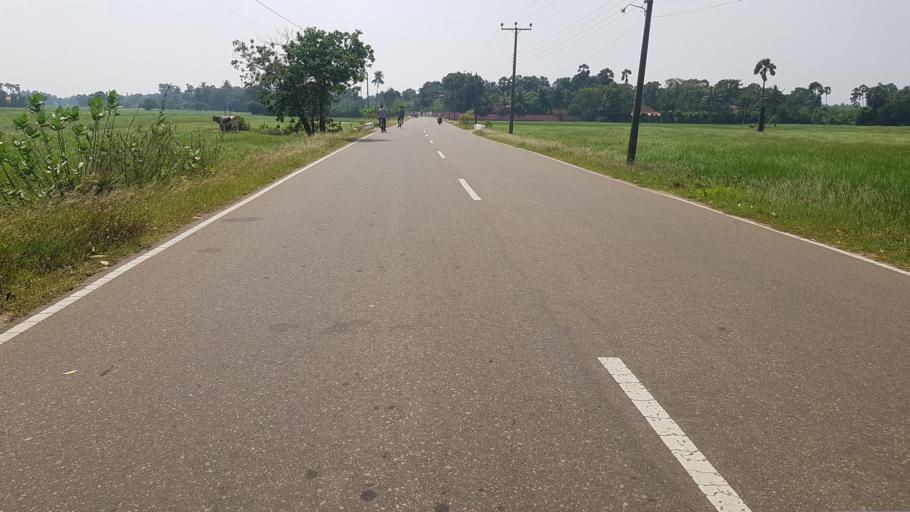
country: LK
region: Northern Province
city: Jaffna
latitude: 9.7270
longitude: 79.9480
